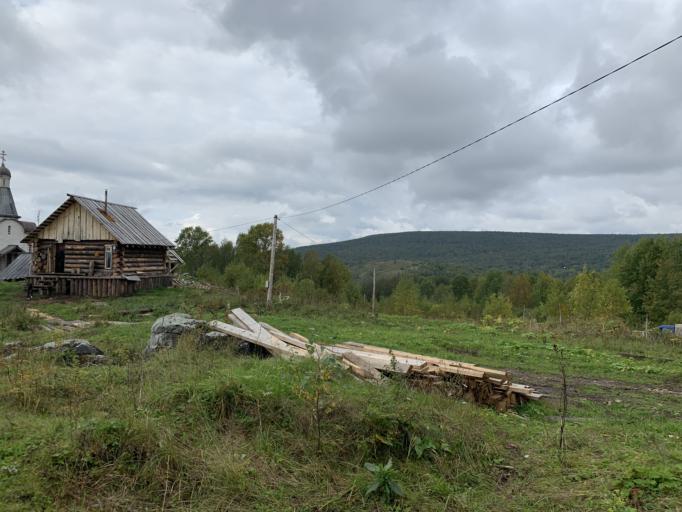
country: RU
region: Perm
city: Gubakha
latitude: 58.8700
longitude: 57.6282
